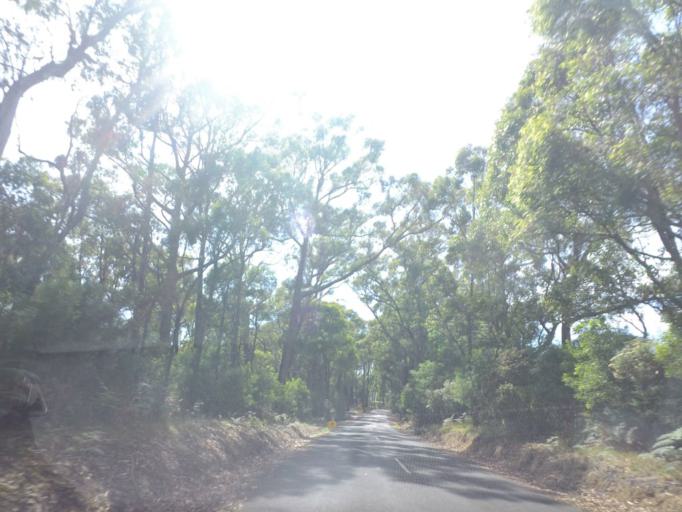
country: AU
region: Victoria
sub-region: Nillumbik
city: Saint Andrews
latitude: -37.5072
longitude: 145.3716
